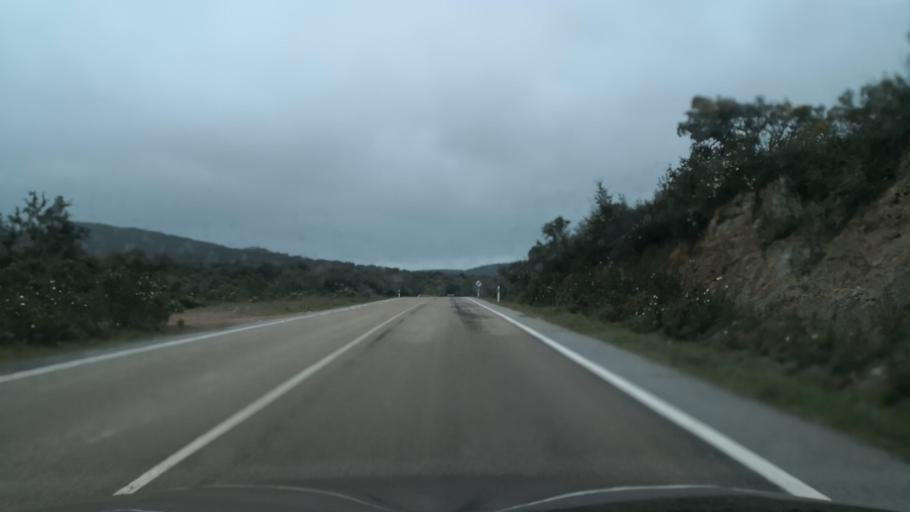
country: ES
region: Extremadura
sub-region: Provincia de Caceres
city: Malpartida de Caceres
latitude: 39.3021
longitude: -6.5157
